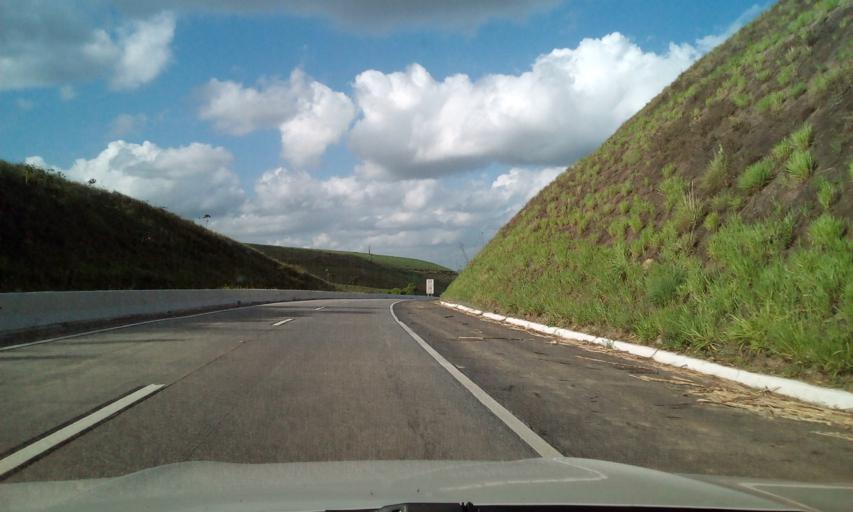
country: BR
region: Pernambuco
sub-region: Palmares
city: Palmares
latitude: -8.6567
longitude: -35.5650
